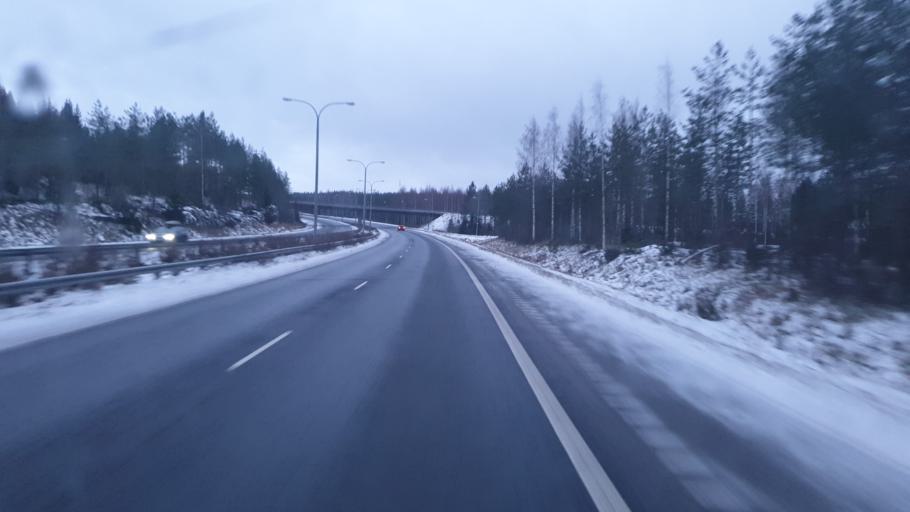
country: FI
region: Northern Savo
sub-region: Kuopio
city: Siilinjaervi
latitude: 63.0199
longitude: 27.6613
